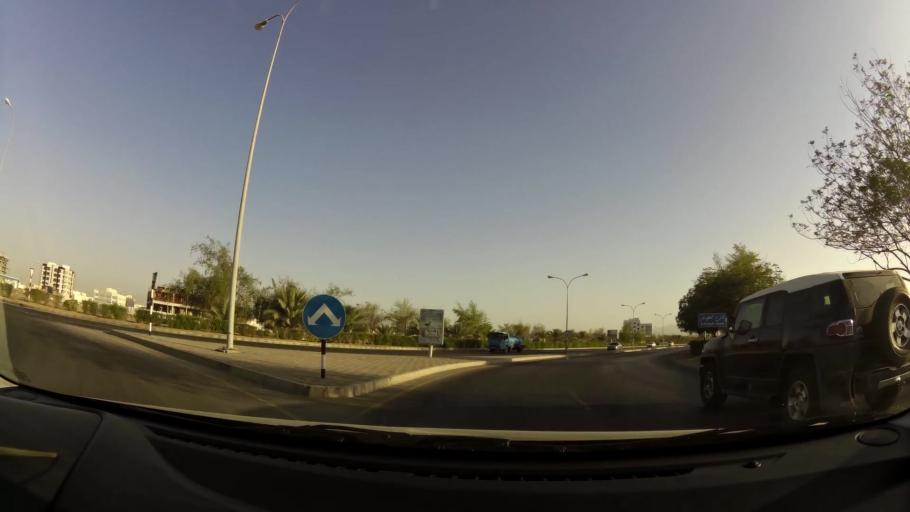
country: OM
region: Muhafazat Masqat
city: As Sib al Jadidah
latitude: 23.6181
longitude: 58.1799
